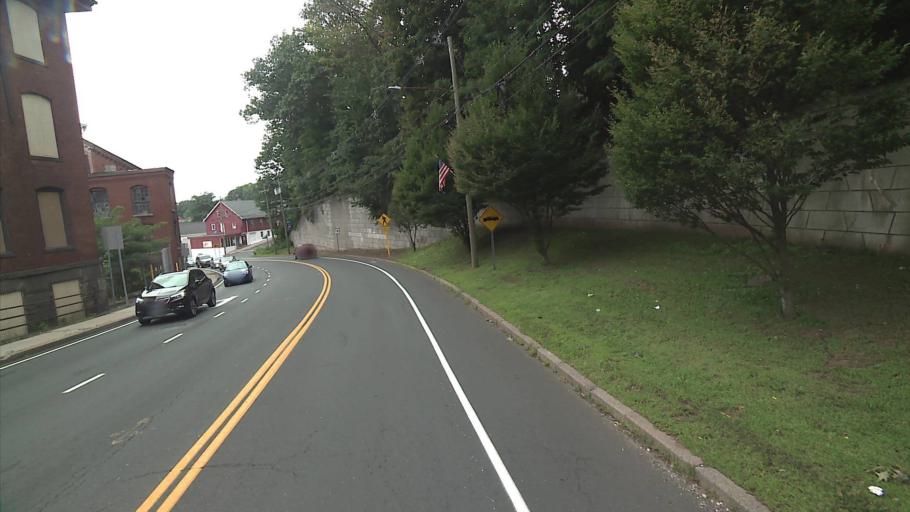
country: US
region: Connecticut
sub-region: Tolland County
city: Rockville
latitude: 41.8677
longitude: -72.4425
